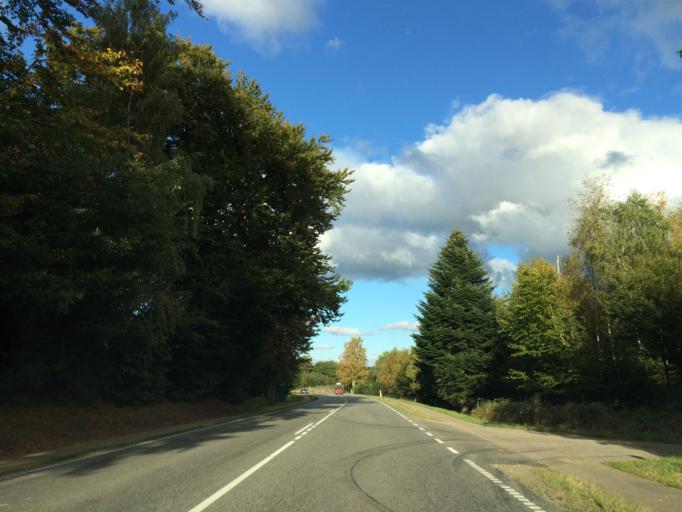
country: DK
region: Central Jutland
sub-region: Skanderborg Kommune
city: Ry
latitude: 56.0882
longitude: 9.7495
